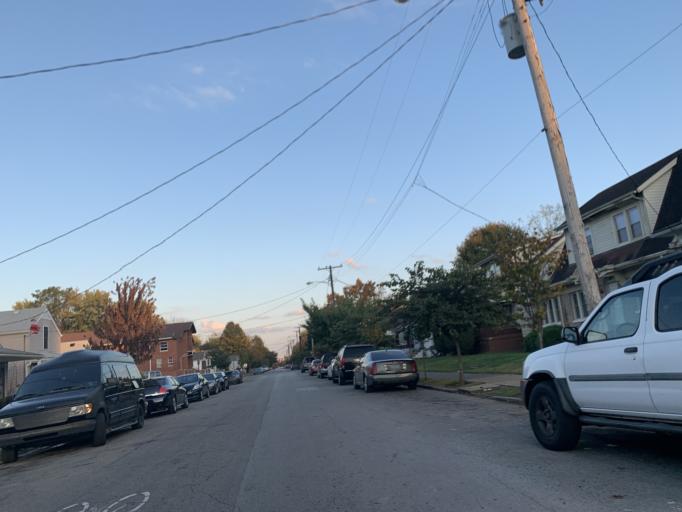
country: US
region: Kentucky
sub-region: Jefferson County
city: Louisville
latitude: 38.2540
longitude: -85.7928
